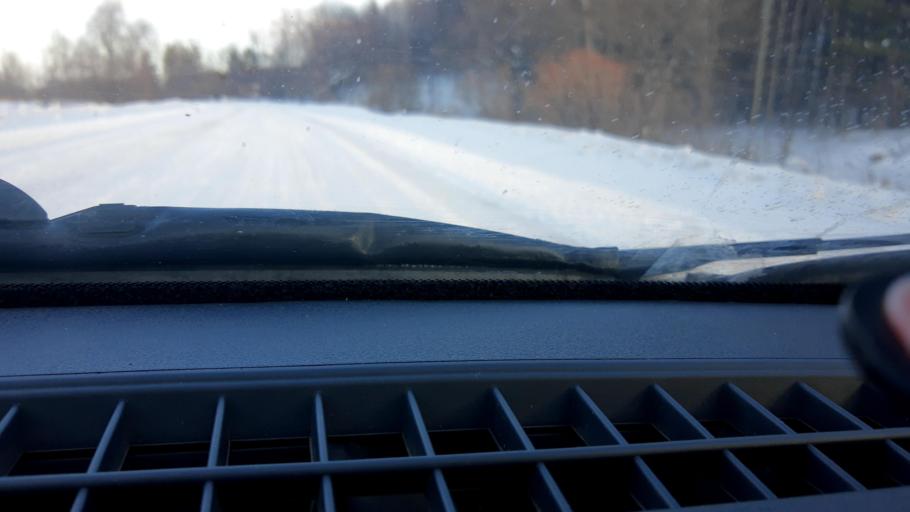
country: RU
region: Bashkortostan
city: Asanovo
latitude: 55.1443
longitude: 55.6413
